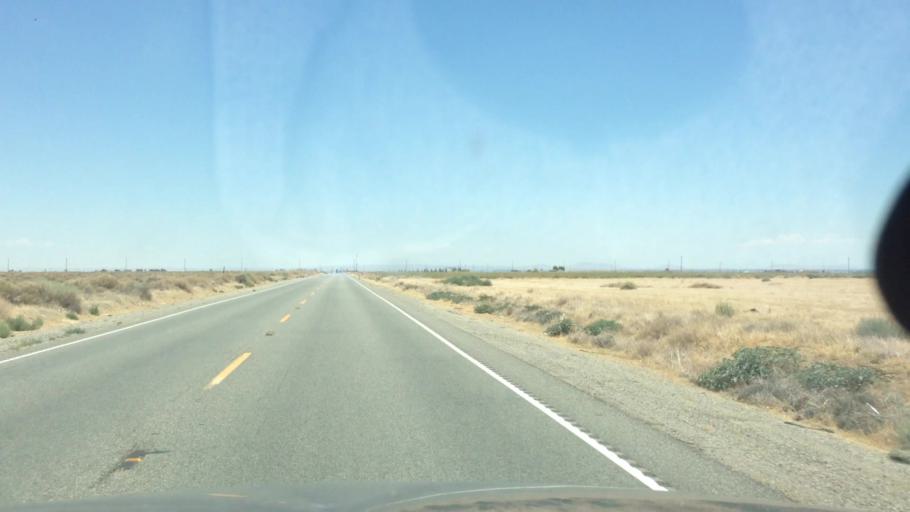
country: US
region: California
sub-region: Kern County
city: Rosamond
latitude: 34.7765
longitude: -118.2702
